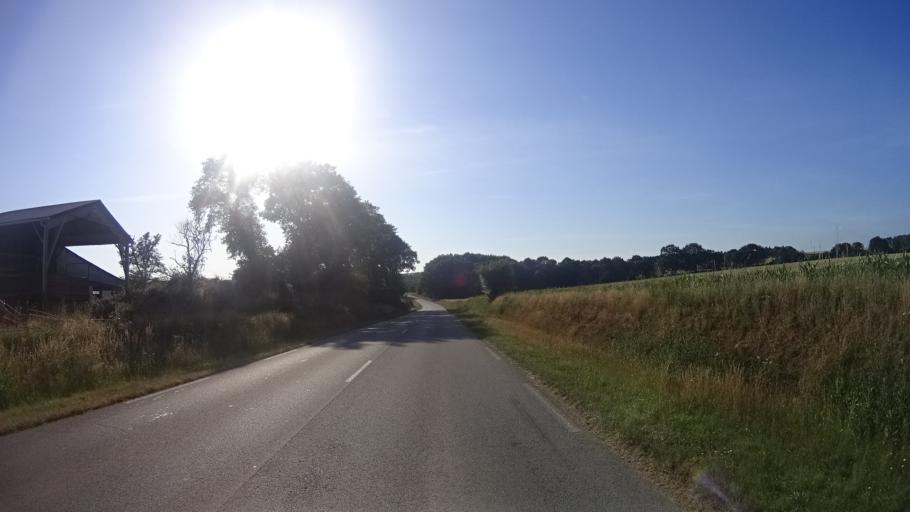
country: FR
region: Brittany
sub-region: Departement du Morbihan
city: Rieux
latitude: 47.6071
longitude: -2.1292
